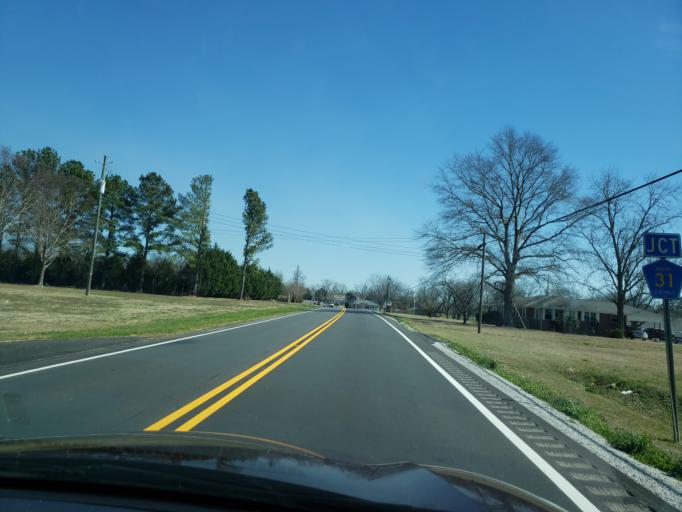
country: US
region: Alabama
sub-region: Elmore County
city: Tallassee
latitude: 32.5823
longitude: -85.7418
